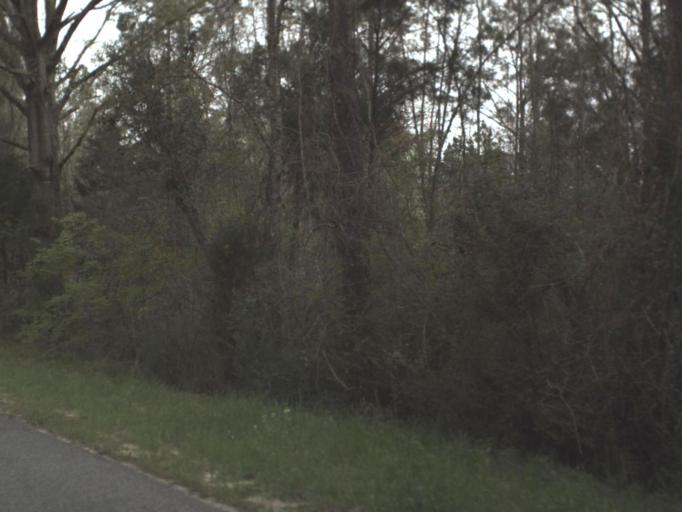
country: US
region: Florida
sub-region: Holmes County
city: Bonifay
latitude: 30.8482
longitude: -85.6667
